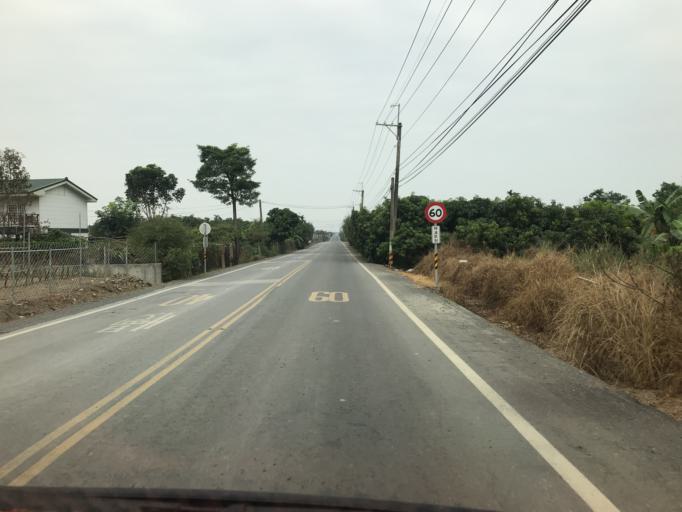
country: TW
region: Taiwan
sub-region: Pingtung
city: Pingtung
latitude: 22.4575
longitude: 120.6140
